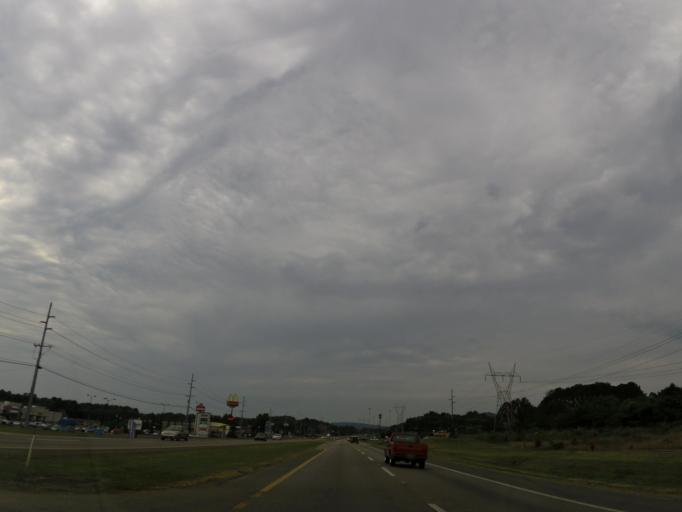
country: US
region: Alabama
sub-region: Jackson County
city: Scottsboro
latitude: 34.6504
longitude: -86.0288
